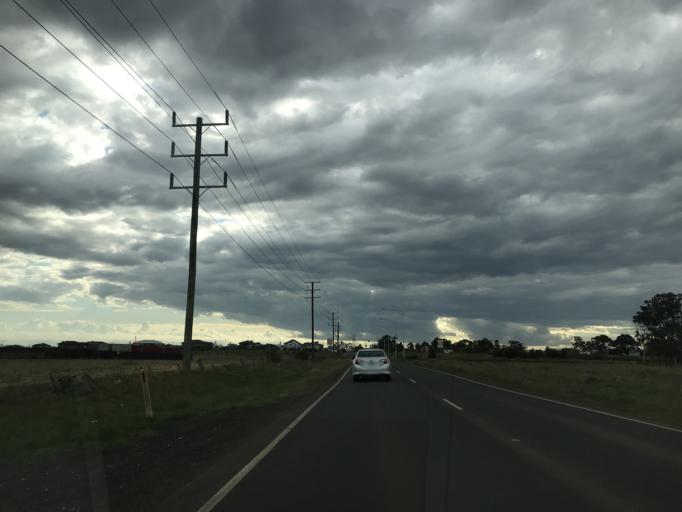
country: AU
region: Victoria
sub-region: Wyndham
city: Truganina
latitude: -37.8238
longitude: 144.7345
